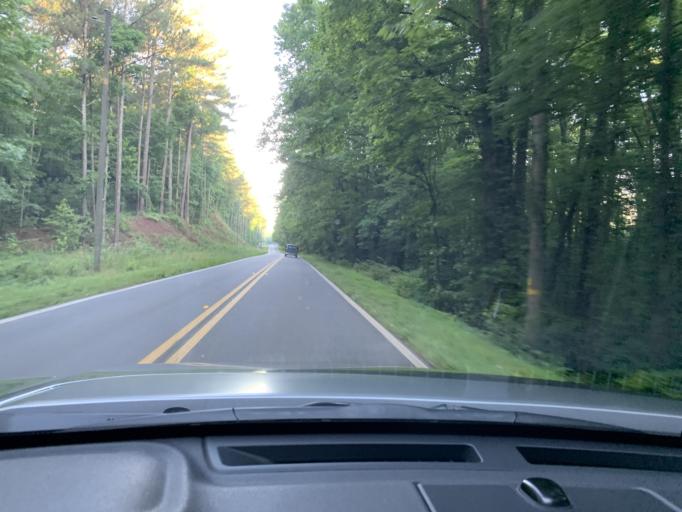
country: US
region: Georgia
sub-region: Bartow County
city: Rydal
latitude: 34.2733
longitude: -84.7320
